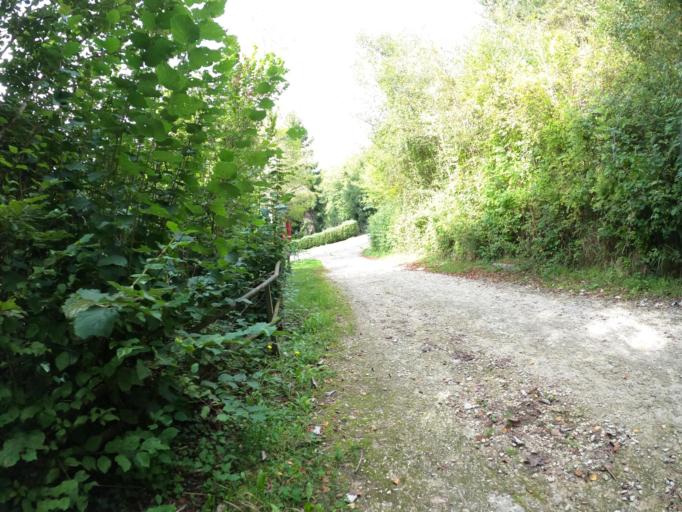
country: ES
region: Navarre
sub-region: Provincia de Navarra
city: Lekunberri
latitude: 43.0076
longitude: -1.8936
